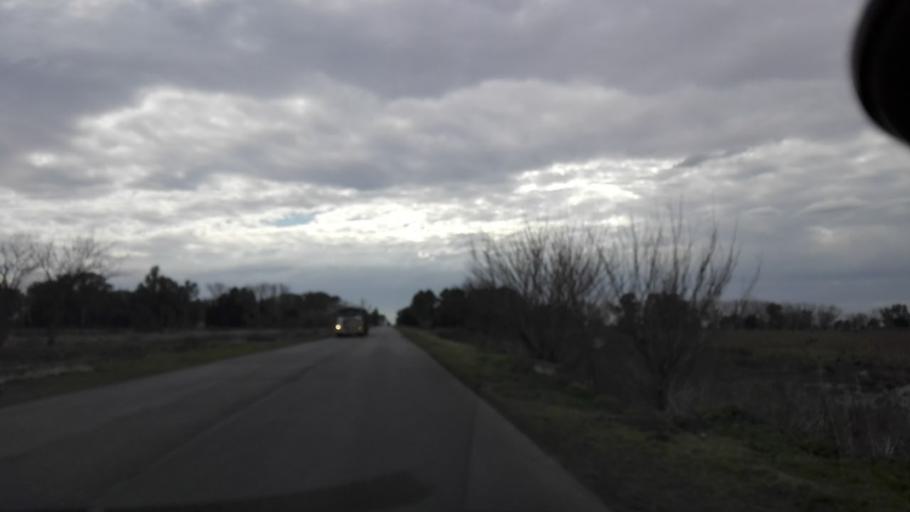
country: AR
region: Buenos Aires
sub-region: Partido de Las Flores
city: Las Flores
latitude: -36.2236
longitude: -59.0446
